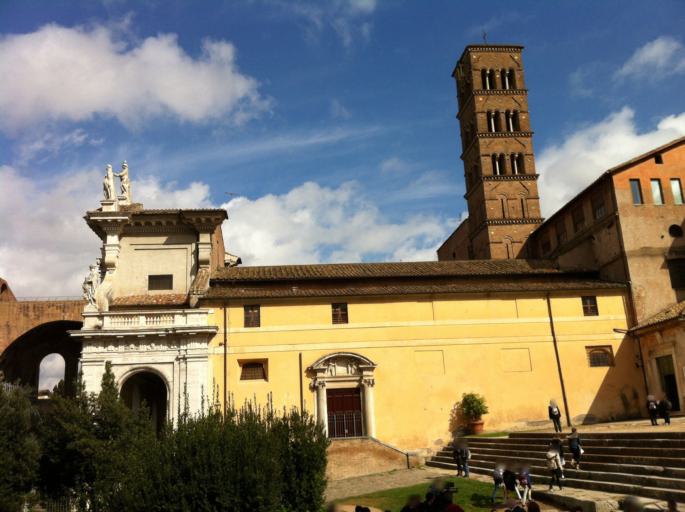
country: IT
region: Latium
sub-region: Citta metropolitana di Roma Capitale
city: Rome
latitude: 41.8909
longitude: 12.4884
